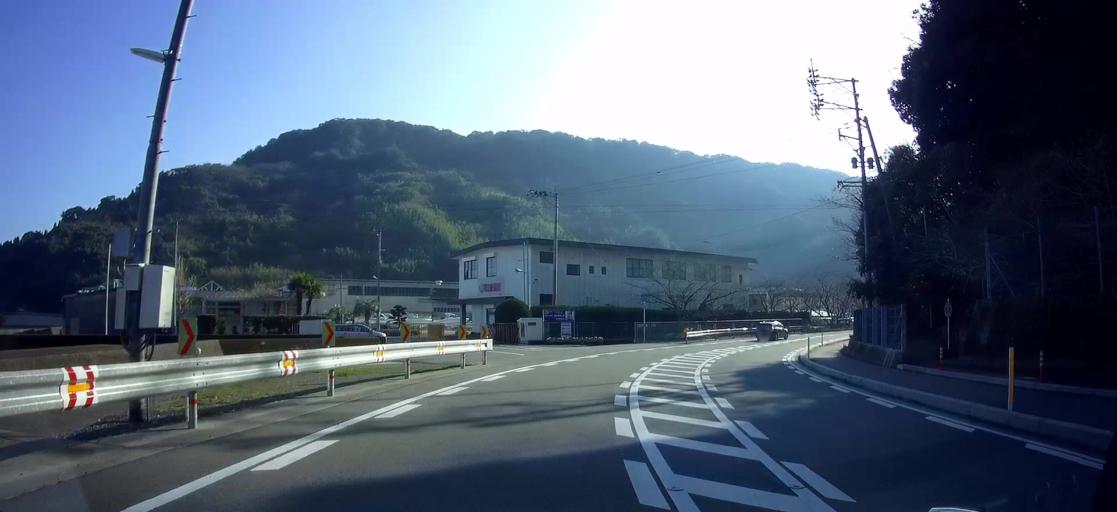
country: JP
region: Kumamoto
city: Minamata
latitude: 32.4196
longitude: 130.4057
